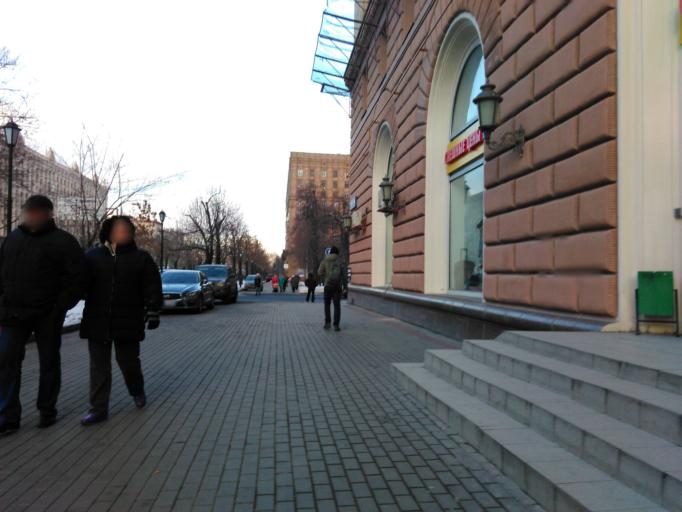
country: RU
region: Moscow
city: Mar'ina Roshcha
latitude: 55.8108
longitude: 37.6382
